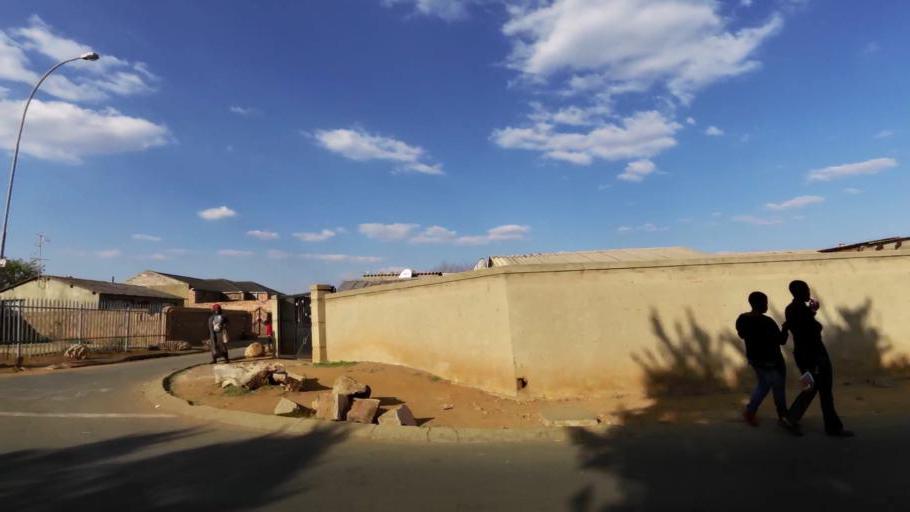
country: ZA
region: Gauteng
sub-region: City of Johannesburg Metropolitan Municipality
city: Roodepoort
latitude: -26.2105
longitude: 27.8771
